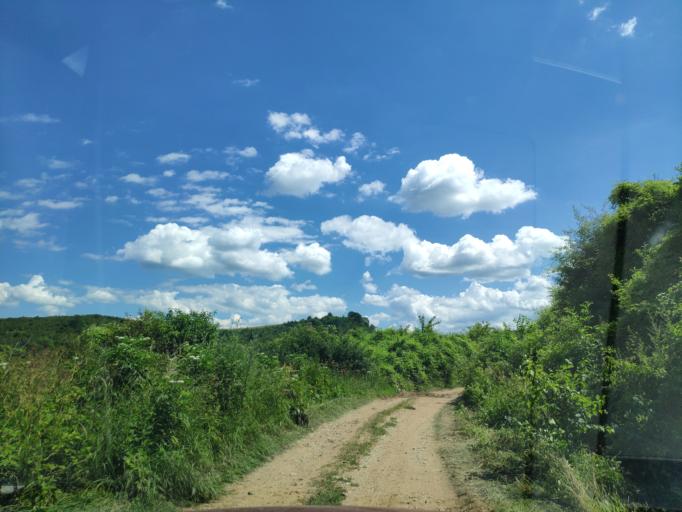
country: HU
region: Borsod-Abauj-Zemplen
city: Arlo
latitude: 48.2761
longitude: 20.1988
